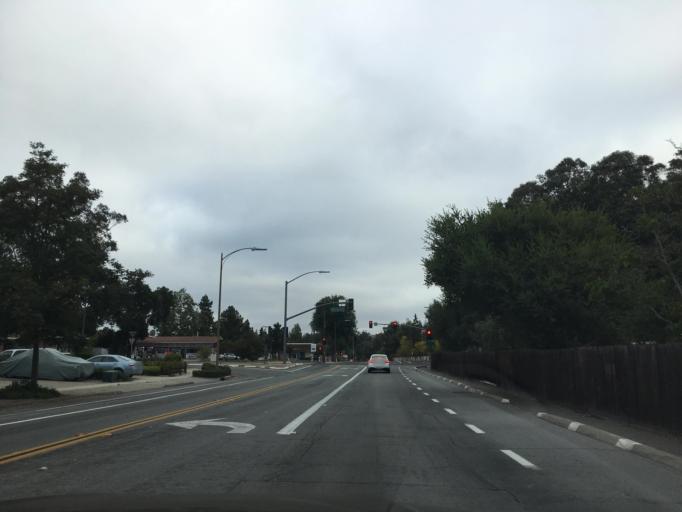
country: US
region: California
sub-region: Santa Clara County
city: Cambrian Park
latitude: 37.2273
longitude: -121.8846
